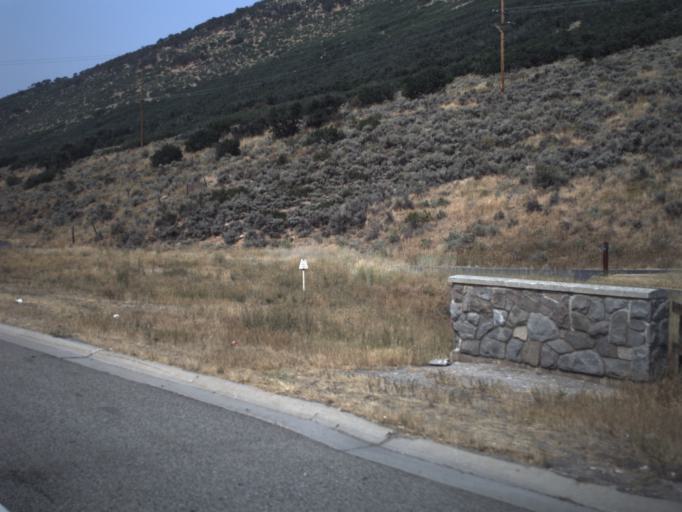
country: US
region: Utah
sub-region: Summit County
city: Snyderville
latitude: 40.6783
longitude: -111.5260
